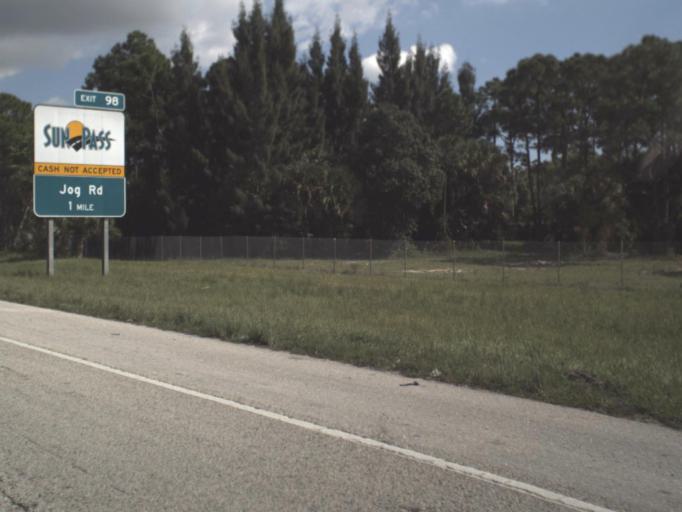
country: US
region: Florida
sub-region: Palm Beach County
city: Lake Belvedere Estates
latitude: 26.6858
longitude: -80.1618
